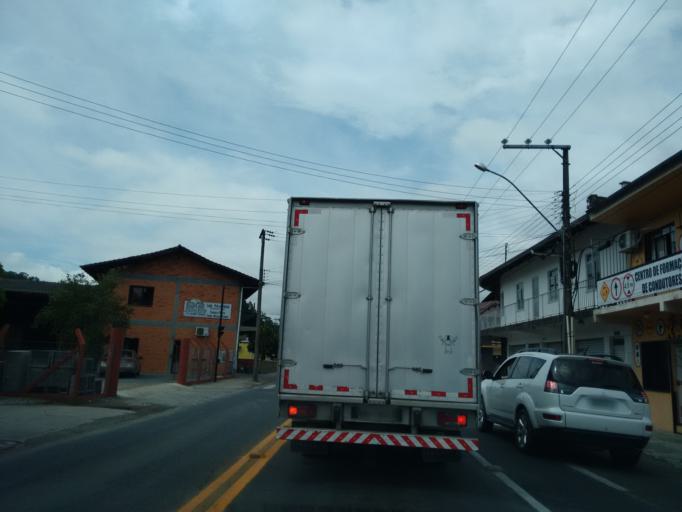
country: BR
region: Santa Catarina
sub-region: Pomerode
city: Pomerode
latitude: -26.7255
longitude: -49.1706
